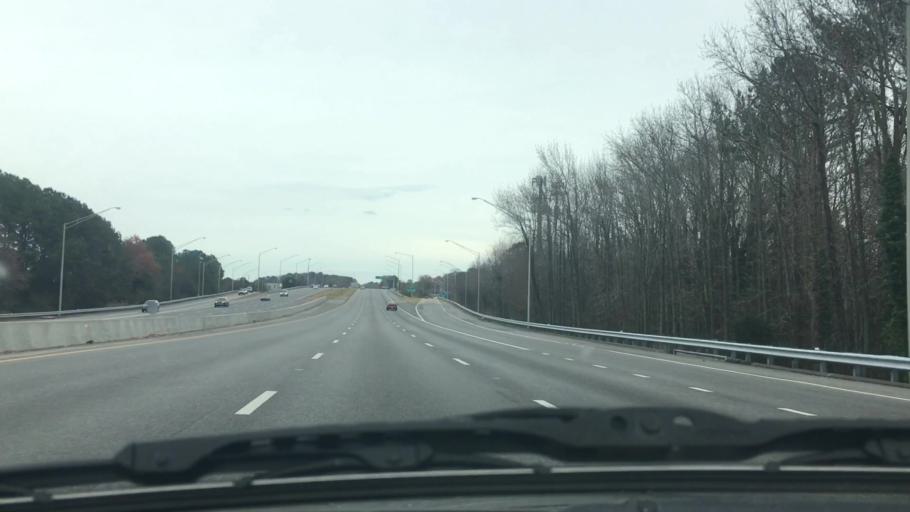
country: US
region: Virginia
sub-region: City of Virginia Beach
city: Virginia Beach
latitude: 36.8442
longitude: -76.0264
